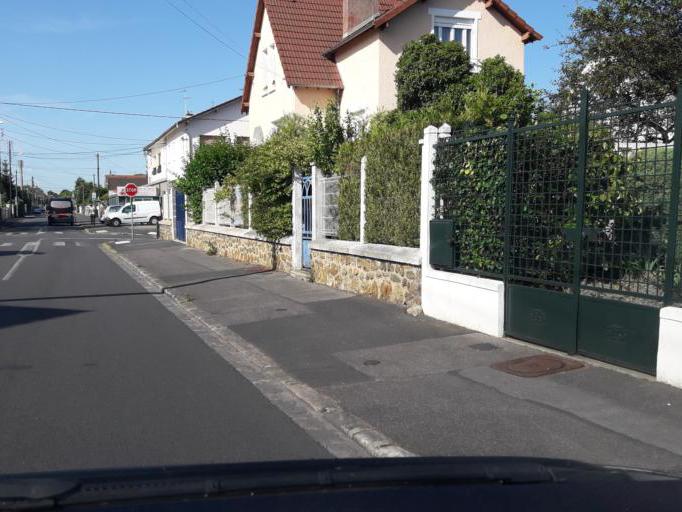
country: FR
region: Ile-de-France
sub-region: Departement de l'Essonne
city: Sainte-Genevieve-des-Bois
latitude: 48.6480
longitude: 2.3305
